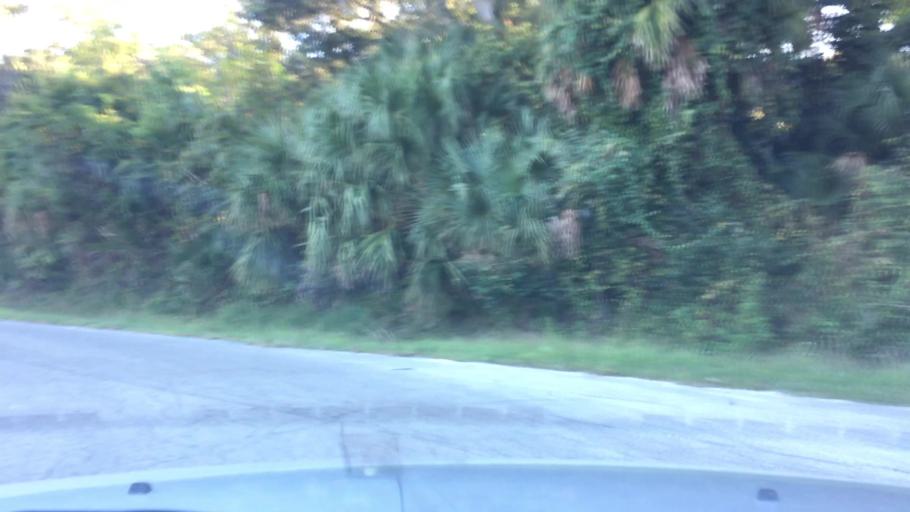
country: US
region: Florida
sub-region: Volusia County
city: Ormond Beach
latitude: 29.2622
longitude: -81.0528
